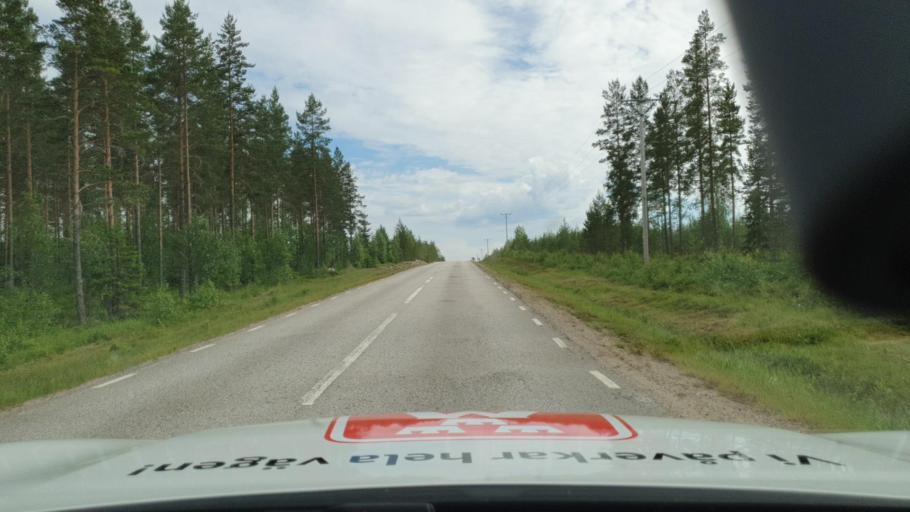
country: NO
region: Hedmark
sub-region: Trysil
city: Innbygda
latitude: 60.9863
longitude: 12.4927
